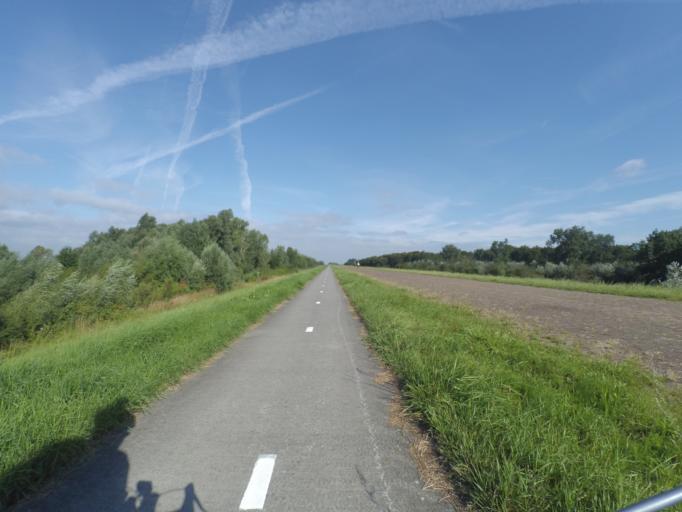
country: NL
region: Flevoland
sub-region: Gemeente Lelystad
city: Lelystad
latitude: 52.4493
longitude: 5.4310
